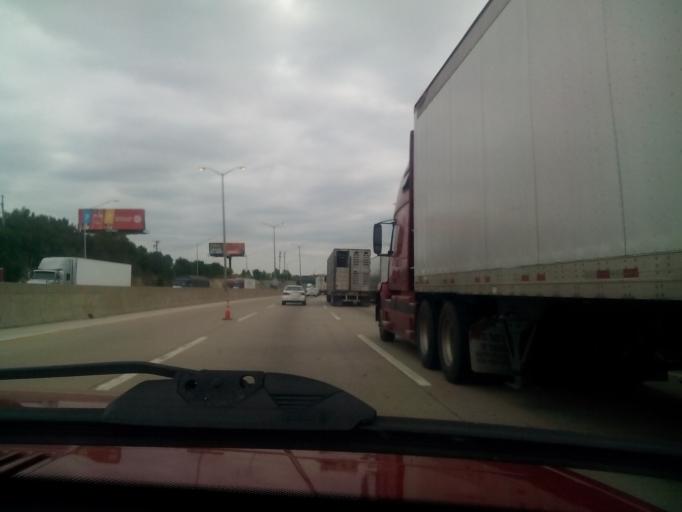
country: US
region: Illinois
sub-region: Cook County
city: East Hazel Crest
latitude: 41.5791
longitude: -87.6287
